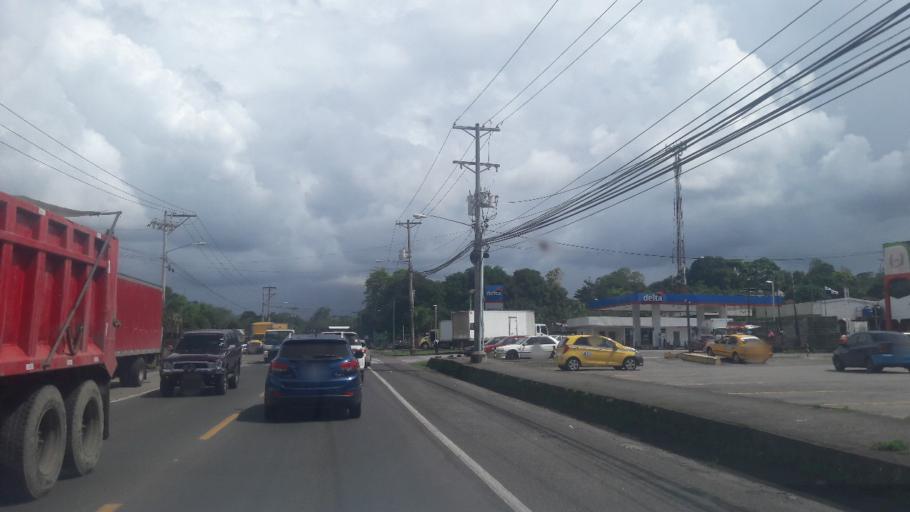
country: PA
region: Panama
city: Alcalde Diaz
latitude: 9.1229
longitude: -79.5941
